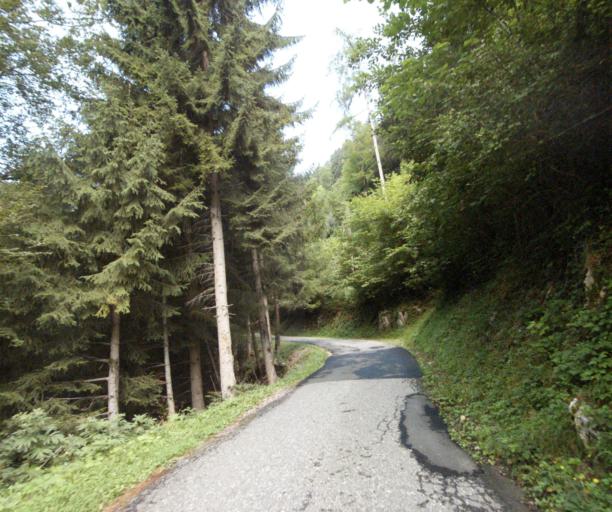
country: CH
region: Vaud
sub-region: Riviera-Pays-d'Enhaut District
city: Caux
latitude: 46.4125
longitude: 6.9526
